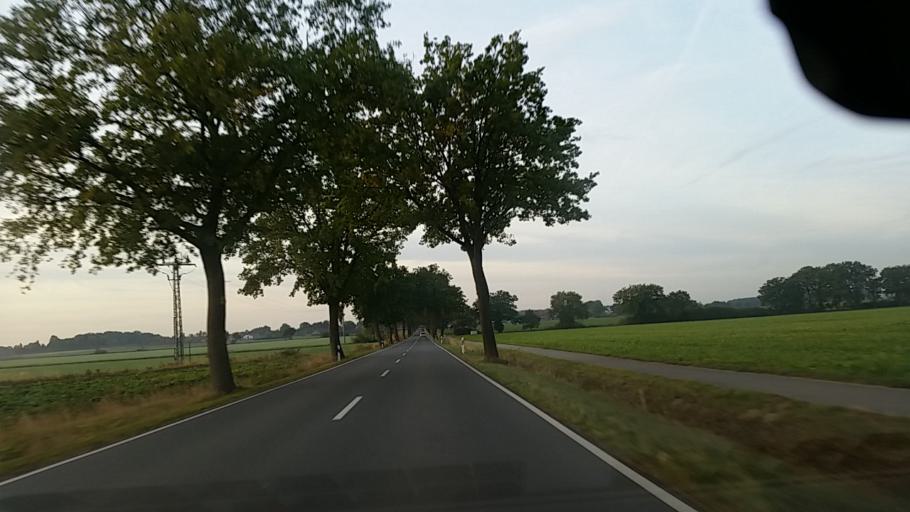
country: DE
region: Lower Saxony
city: Tiddische
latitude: 52.5112
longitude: 10.8043
